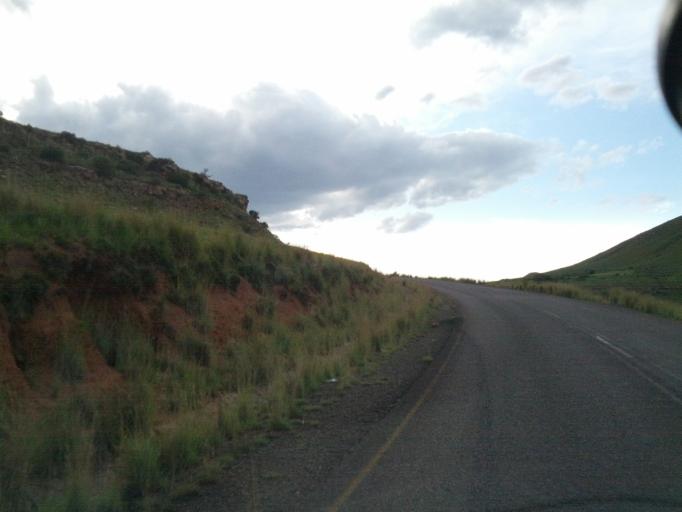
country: LS
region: Qacha's Nek
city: Qacha's Nek
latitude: -30.0533
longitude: 28.5027
